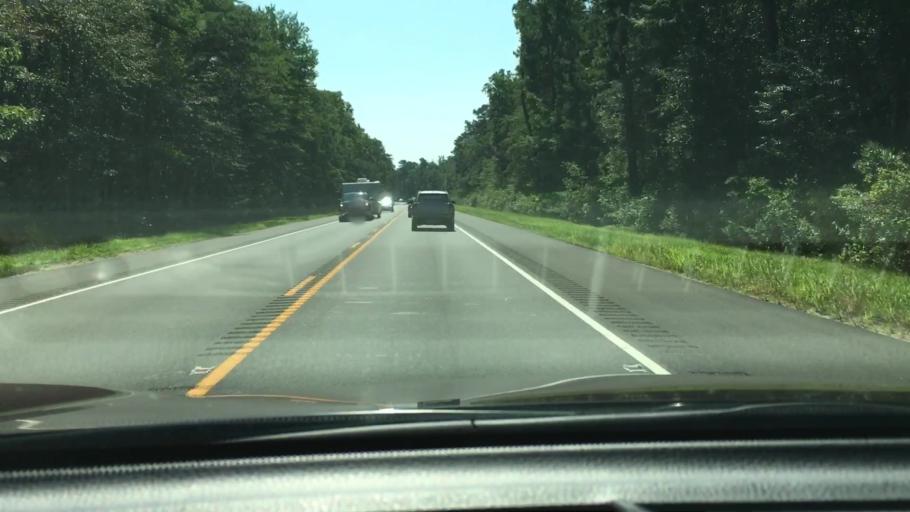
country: US
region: New Jersey
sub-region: Cape May County
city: Woodbine
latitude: 39.3269
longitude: -74.8696
